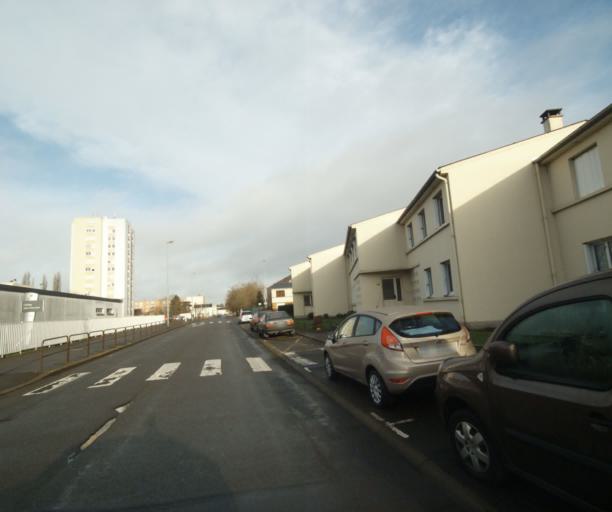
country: FR
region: Pays de la Loire
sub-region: Departement de la Sarthe
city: Le Mans
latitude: 47.9873
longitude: 0.2163
